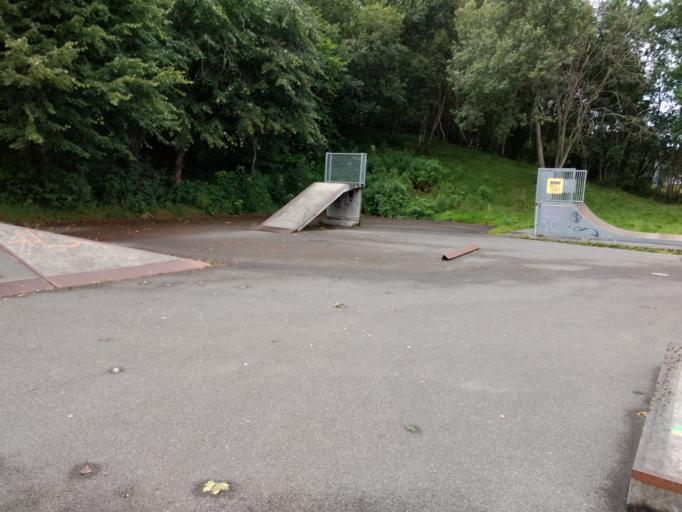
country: NO
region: Rogaland
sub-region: Stavanger
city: Stavanger
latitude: 58.9162
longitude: 5.7211
